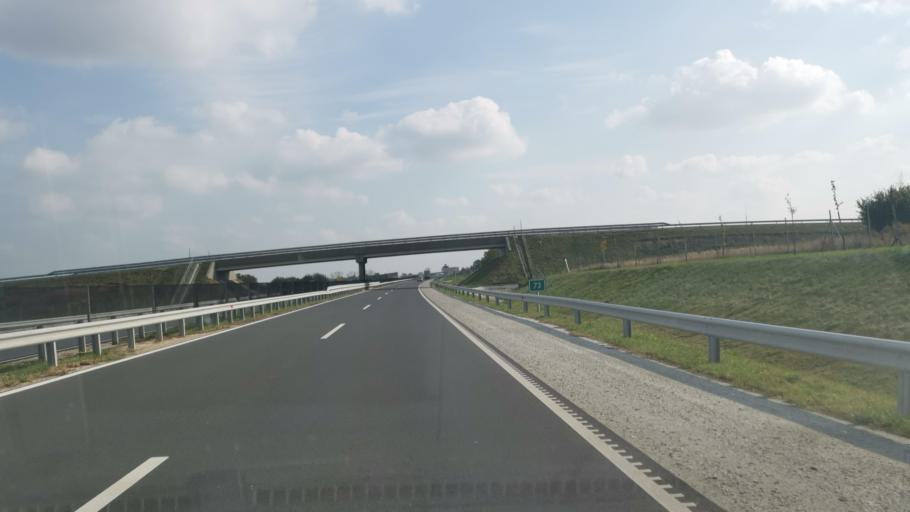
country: HU
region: Gyor-Moson-Sopron
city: Nagycenk
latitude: 47.5984
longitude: 16.6940
